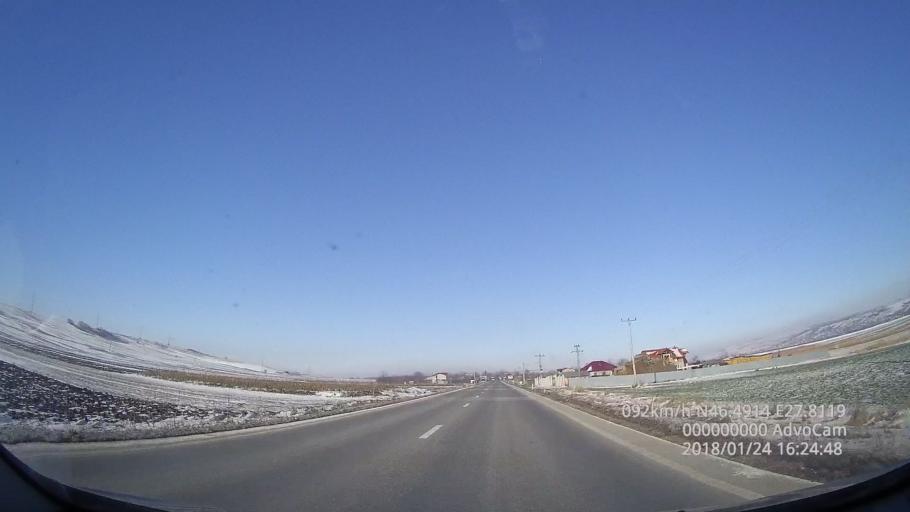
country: RO
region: Vaslui
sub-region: Comuna Albesti
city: Albesti
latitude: 46.4922
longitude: 27.8120
